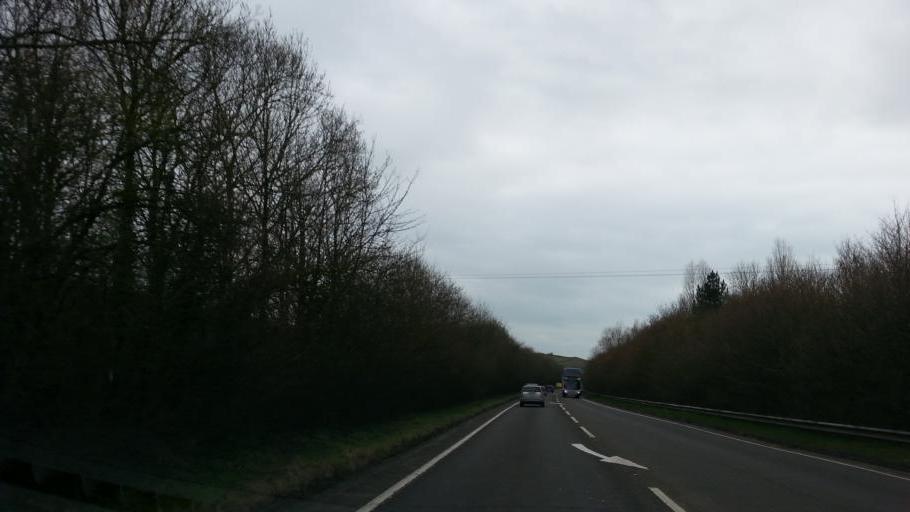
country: GB
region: England
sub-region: Devon
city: Appledore
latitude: 51.0337
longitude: -4.1629
